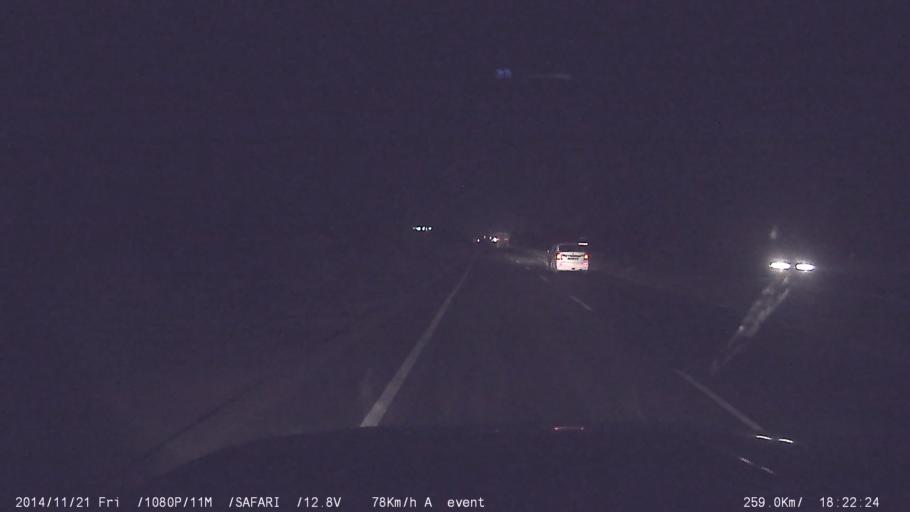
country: IN
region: Tamil Nadu
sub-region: Kancheepuram
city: Kanchipuram
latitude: 12.8734
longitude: 79.6685
